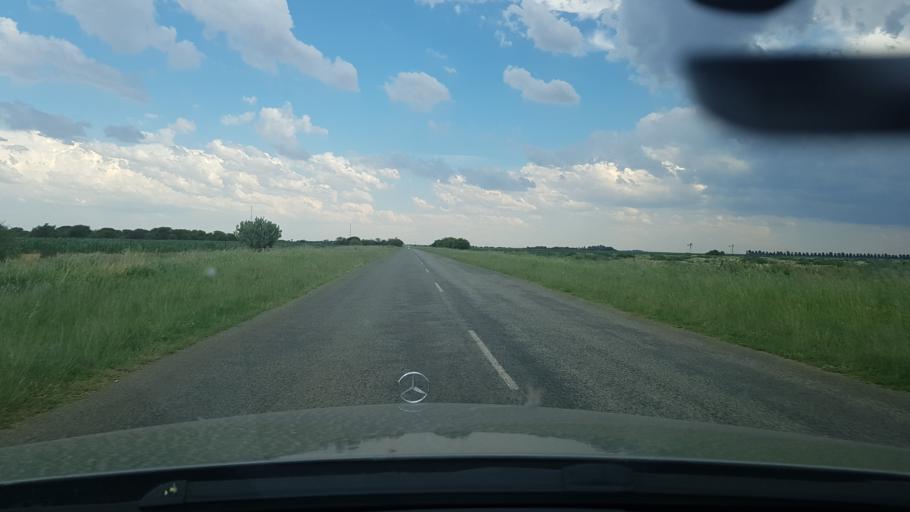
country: ZA
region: Orange Free State
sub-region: Lejweleputswa District Municipality
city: Hoopstad
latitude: -27.9367
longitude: 25.6941
